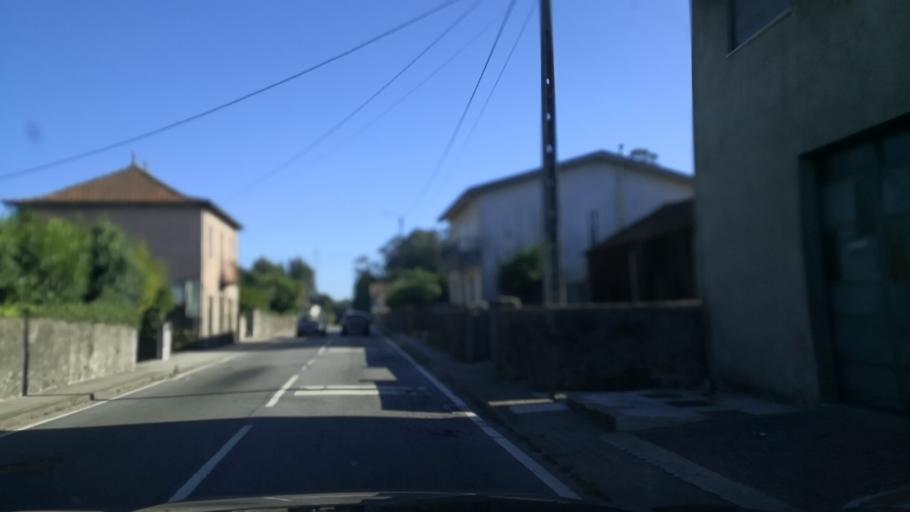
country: PT
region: Porto
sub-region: Santo Tirso
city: Sao Miguel do Couto
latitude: 41.2954
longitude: -8.4711
